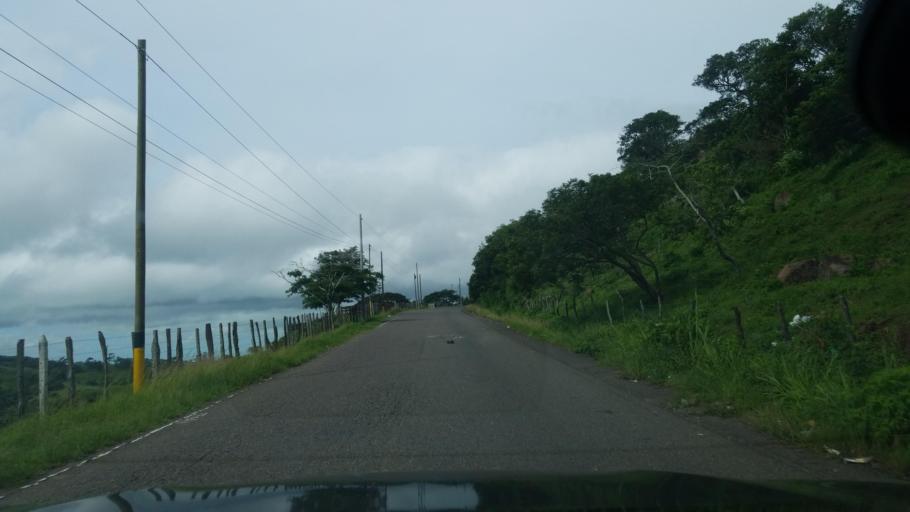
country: HN
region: Choluteca
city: San Marcos de Colon
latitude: 13.3704
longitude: -86.9200
